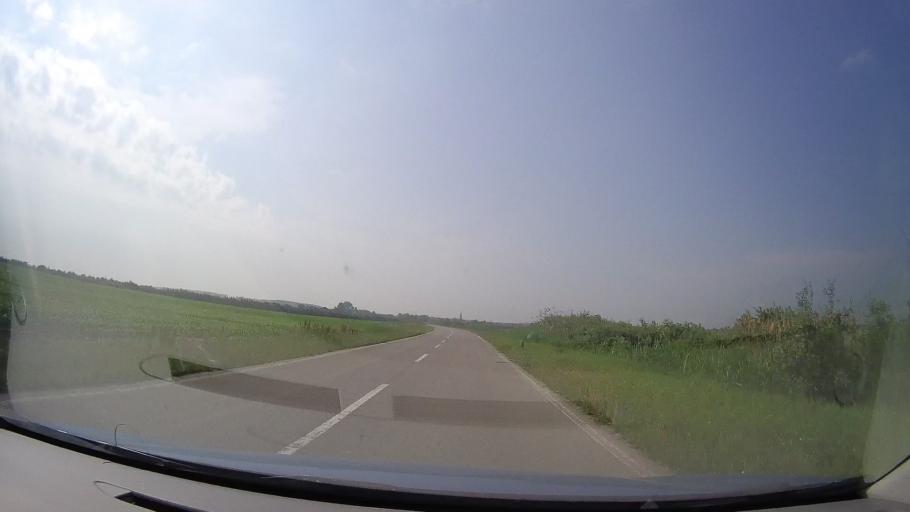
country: RS
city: Jasa Tomic
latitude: 45.4630
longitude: 20.8529
